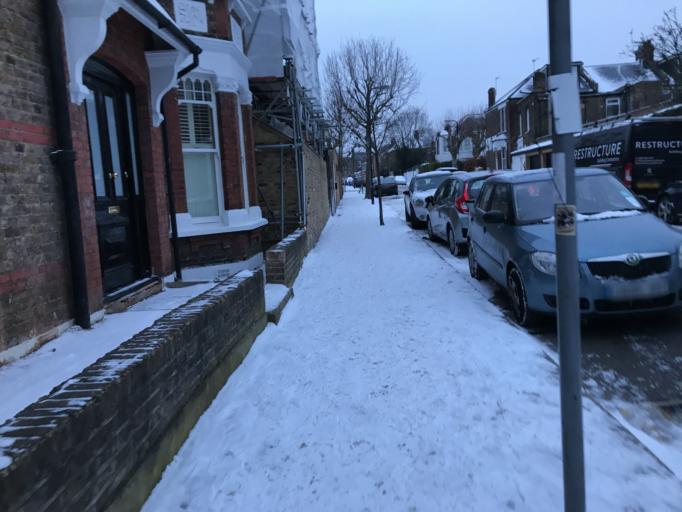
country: GB
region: England
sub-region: Greater London
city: Bayswater
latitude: 51.5338
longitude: -0.2144
